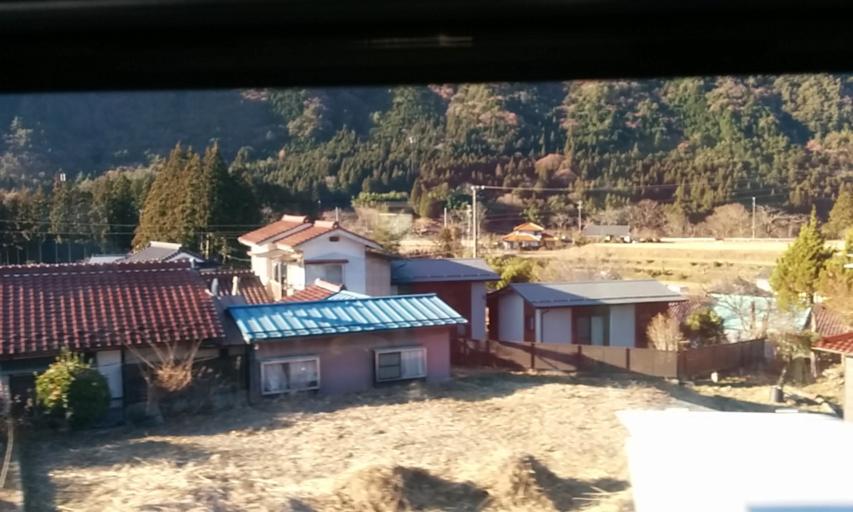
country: JP
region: Gifu
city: Nakatsugawa
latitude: 35.6707
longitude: 137.6330
